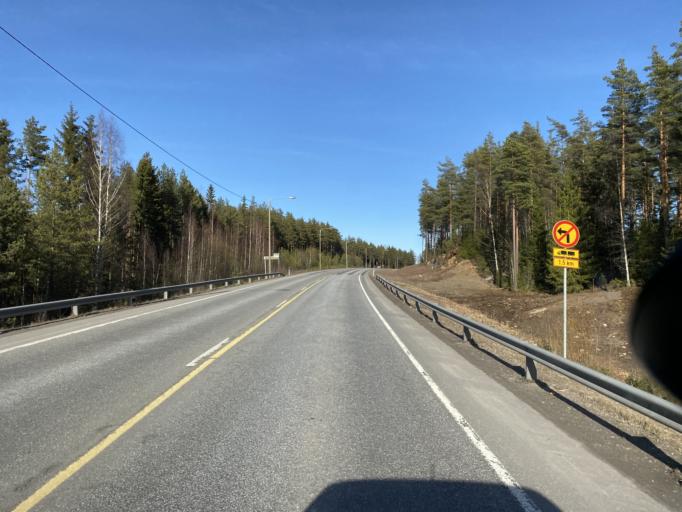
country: FI
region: Satakunta
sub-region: Rauma
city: Eura
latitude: 61.1426
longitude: 22.1925
